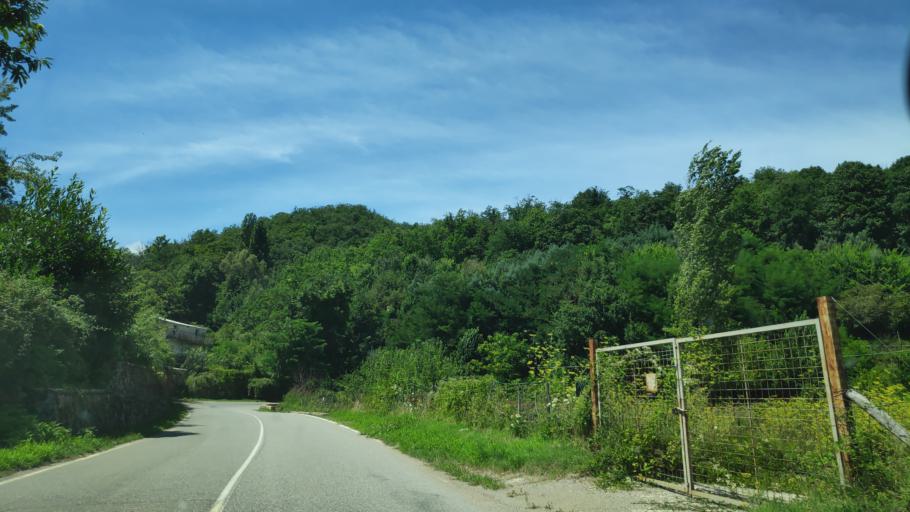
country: IT
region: Calabria
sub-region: Provincia di Catanzaro
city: Palermiti
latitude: 38.7445
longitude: 16.4496
